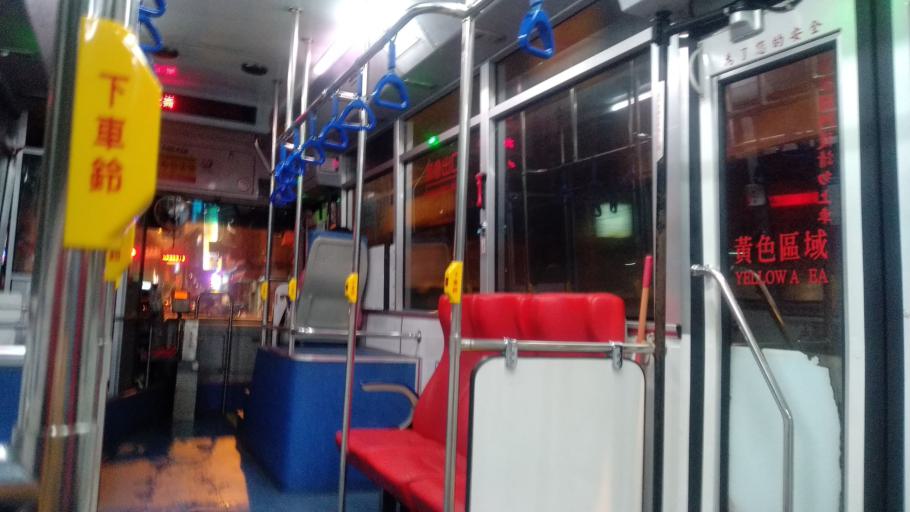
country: TW
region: Taiwan
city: Taoyuan City
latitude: 24.9897
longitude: 121.1783
